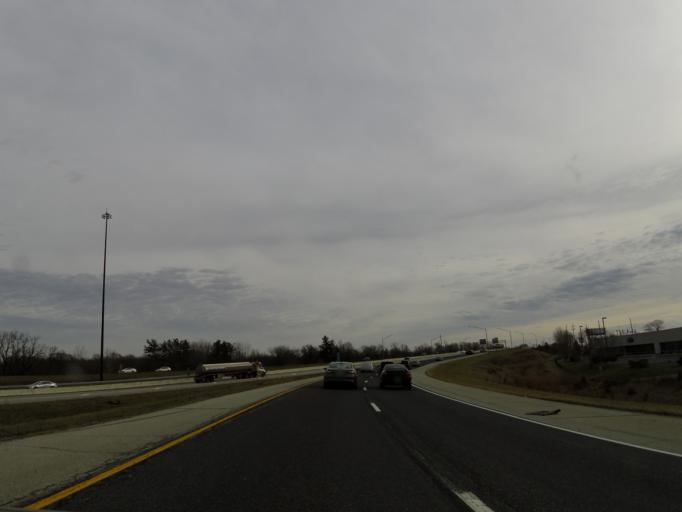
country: US
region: Indiana
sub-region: Boone County
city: Zionsville
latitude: 39.9286
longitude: -86.2645
